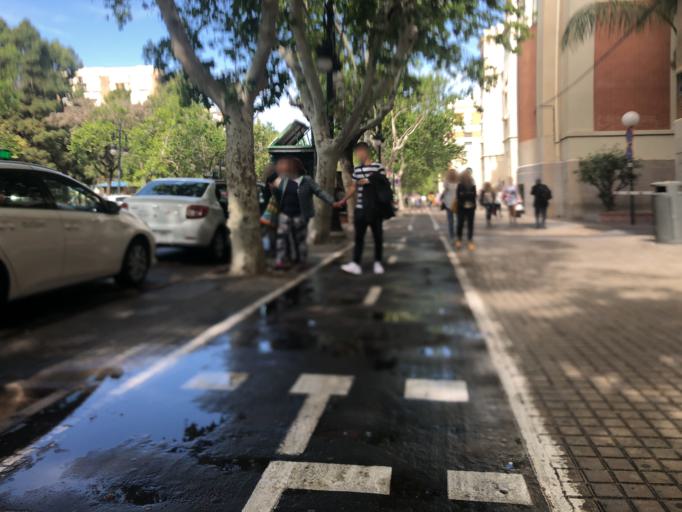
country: ES
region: Valencia
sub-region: Provincia de Valencia
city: Valencia
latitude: 39.4787
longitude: -0.3621
